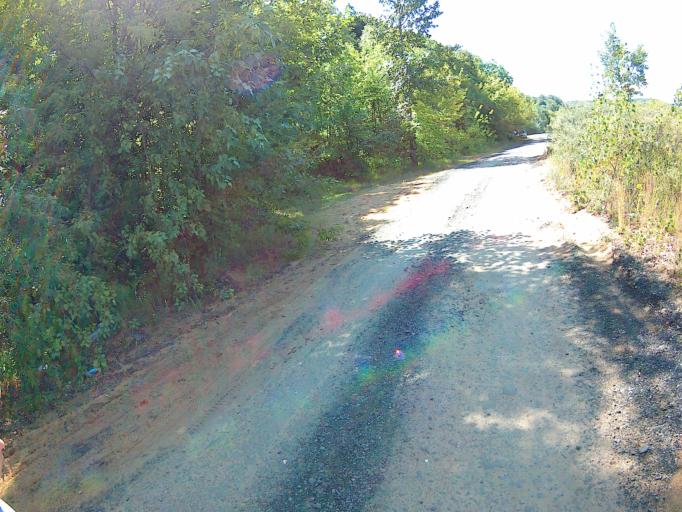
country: RU
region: Nizjnij Novgorod
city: Nizhniy Novgorod
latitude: 56.2631
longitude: 43.9680
